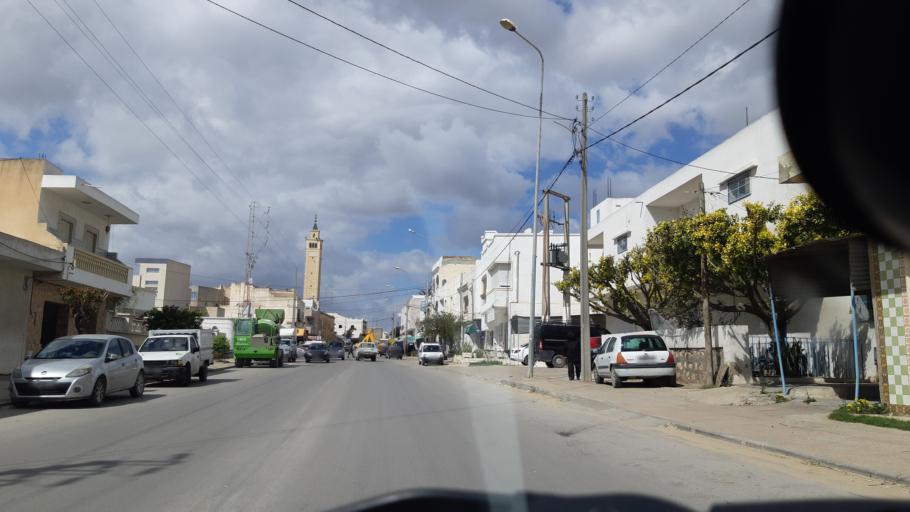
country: TN
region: Susah
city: Akouda
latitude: 35.8727
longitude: 10.5479
